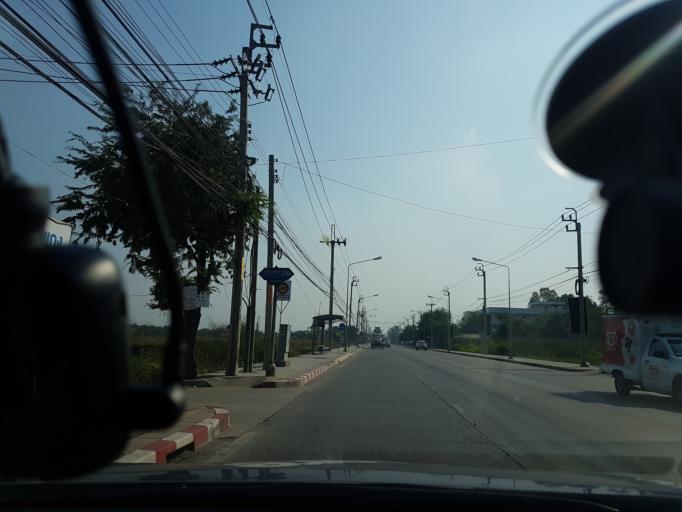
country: TH
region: Bangkok
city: Khlong Sam Wa
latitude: 13.8859
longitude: 100.7223
